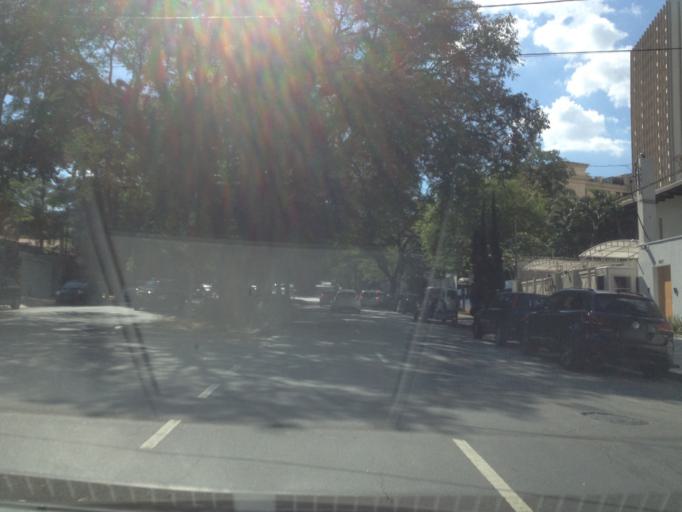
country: BR
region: Sao Paulo
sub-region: Osasco
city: Osasco
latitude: -23.5427
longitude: -46.7190
